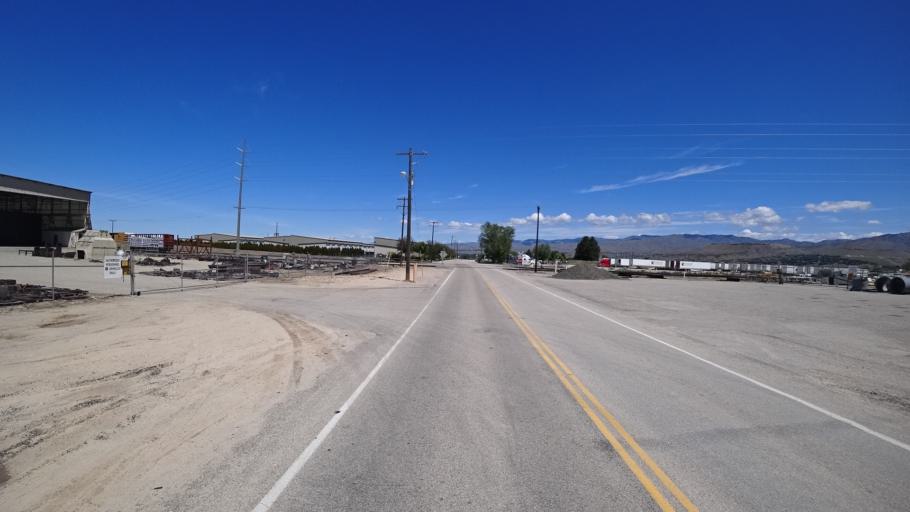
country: US
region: Idaho
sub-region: Ada County
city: Boise
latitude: 43.5626
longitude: -116.1834
